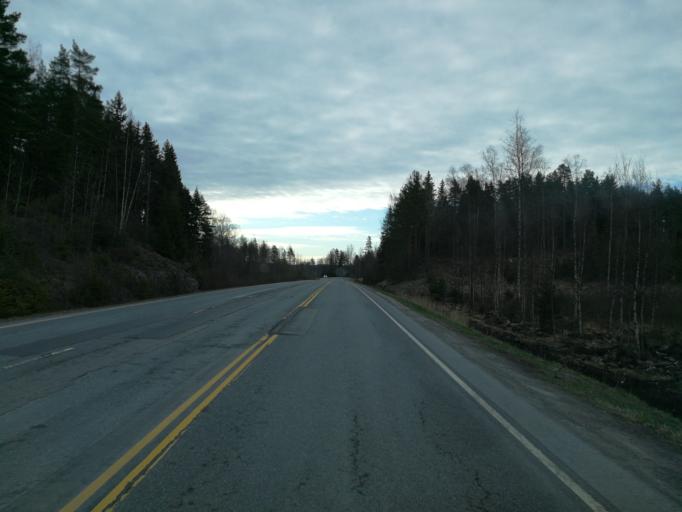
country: FI
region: Varsinais-Suomi
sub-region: Salo
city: Muurla
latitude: 60.3820
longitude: 23.2423
